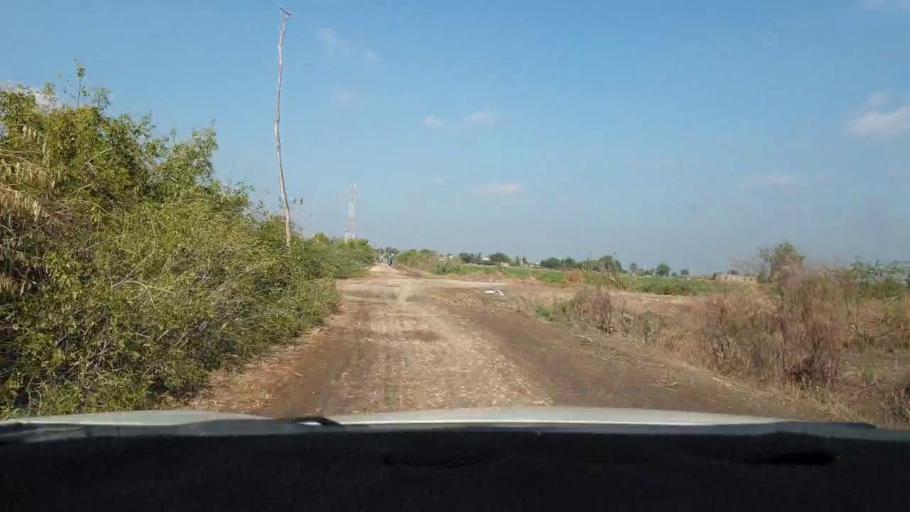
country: PK
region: Sindh
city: Berani
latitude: 25.7731
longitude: 68.8605
